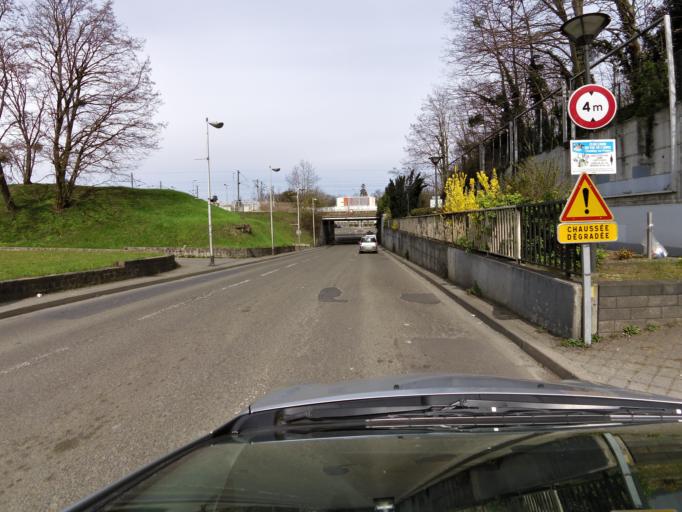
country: FR
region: Ile-de-France
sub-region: Departement de Seine-Saint-Denis
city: Tremblay-en-France
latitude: 48.9440
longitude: 2.5685
